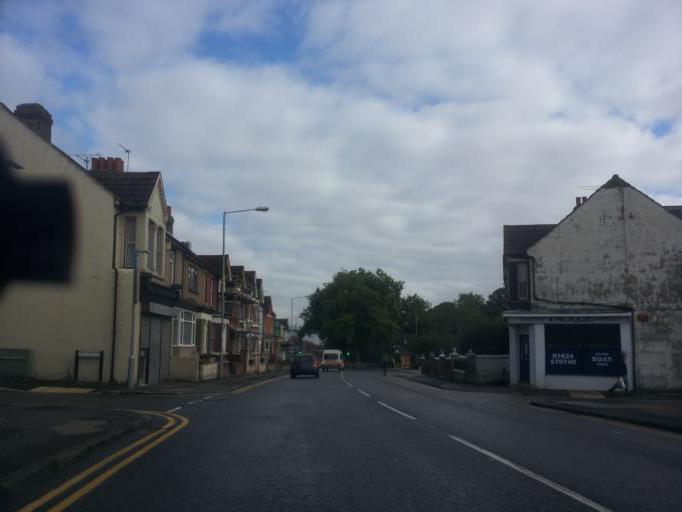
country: GB
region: England
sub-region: Kent
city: Gillingham
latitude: 51.3748
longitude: 0.5522
